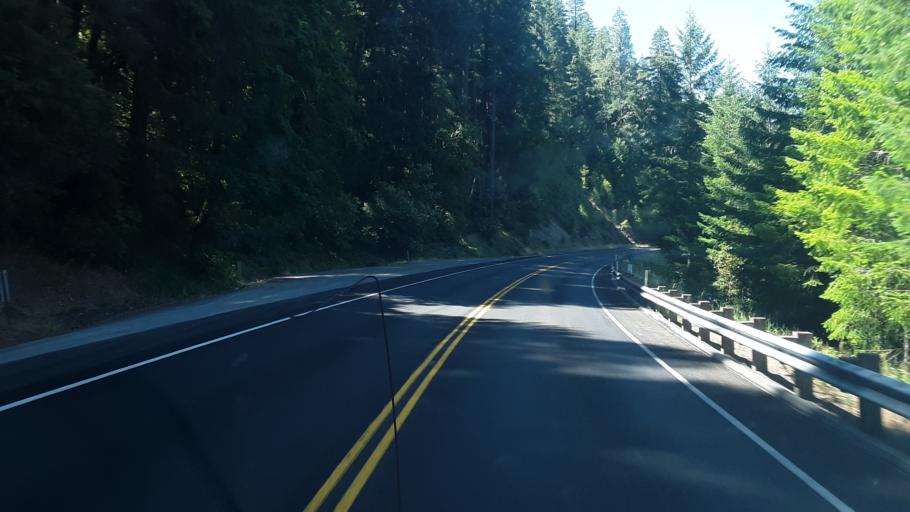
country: US
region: Oregon
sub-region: Josephine County
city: Cave Junction
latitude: 41.9413
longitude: -123.7498
